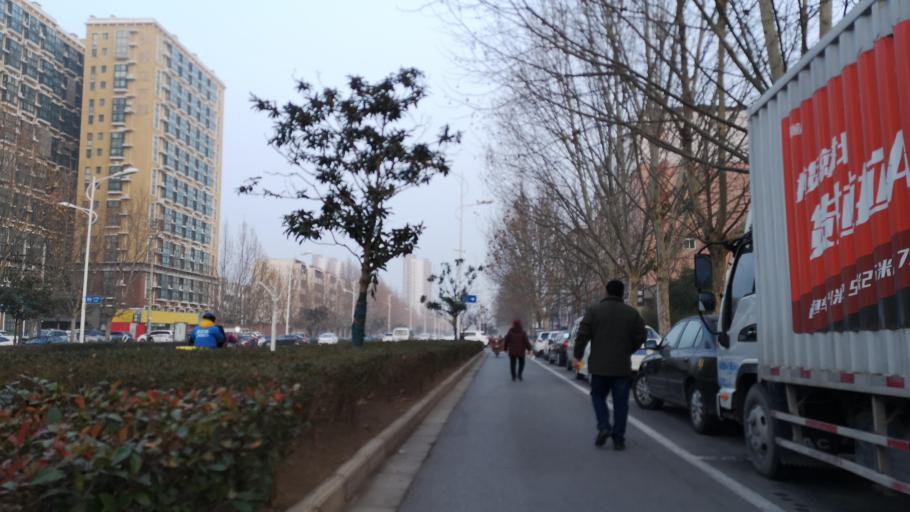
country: CN
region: Henan Sheng
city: Puyang
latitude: 35.7488
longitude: 115.0306
